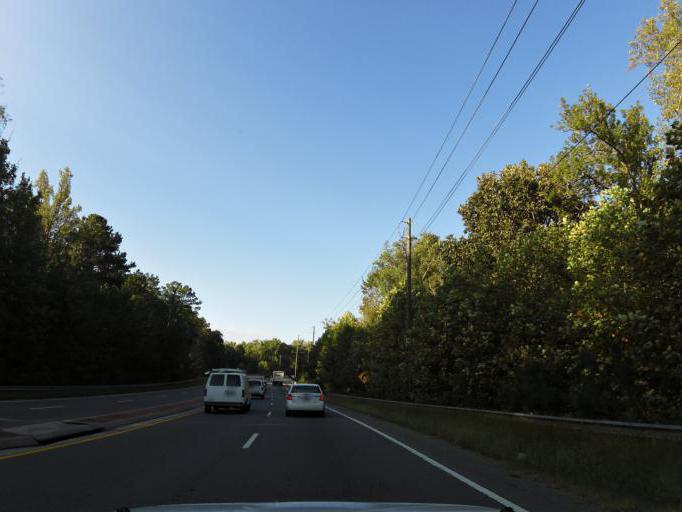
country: US
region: Georgia
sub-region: Cobb County
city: Powder Springs
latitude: 33.8961
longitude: -84.6308
